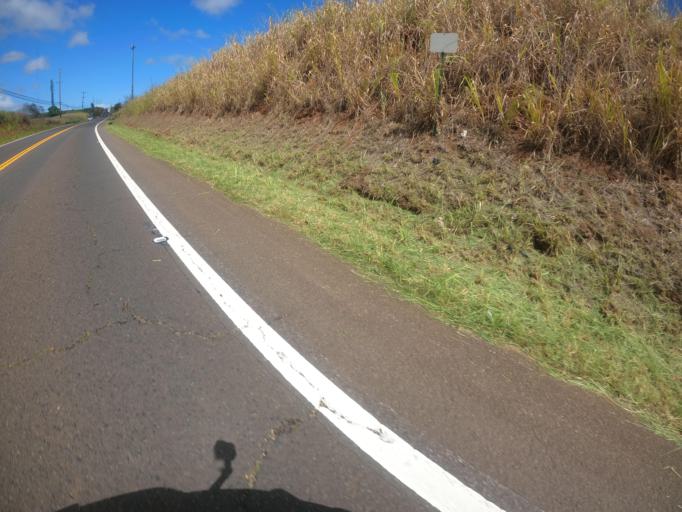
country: US
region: Hawaii
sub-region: Honolulu County
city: Village Park
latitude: 21.4394
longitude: -158.0596
